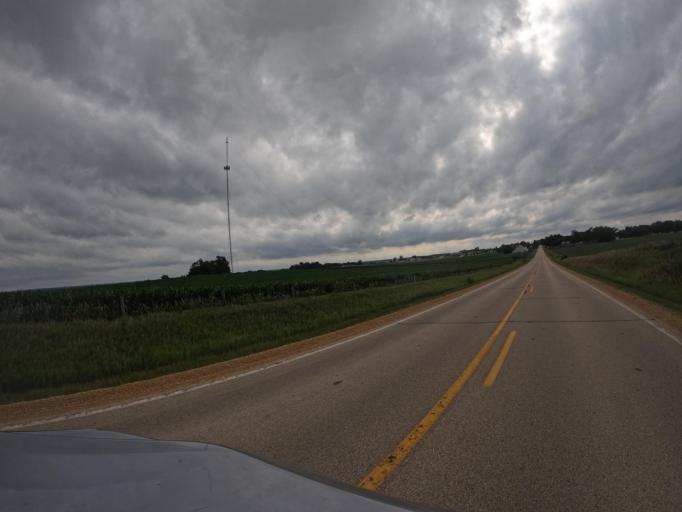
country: US
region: Iowa
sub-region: Clinton County
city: De Witt
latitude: 41.8005
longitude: -90.5323
